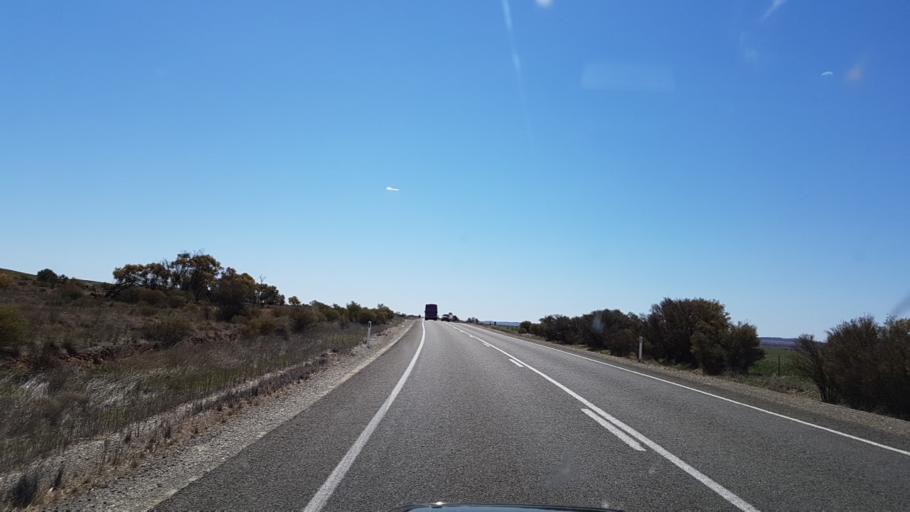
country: AU
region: South Australia
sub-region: Peterborough
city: Peterborough
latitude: -33.2127
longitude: 138.8964
